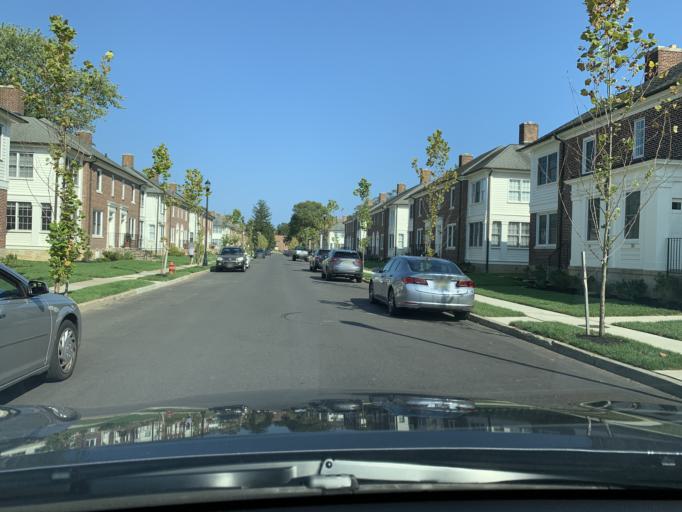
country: US
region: New Jersey
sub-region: Monmouth County
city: Eatontown
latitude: 40.3144
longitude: -74.0394
